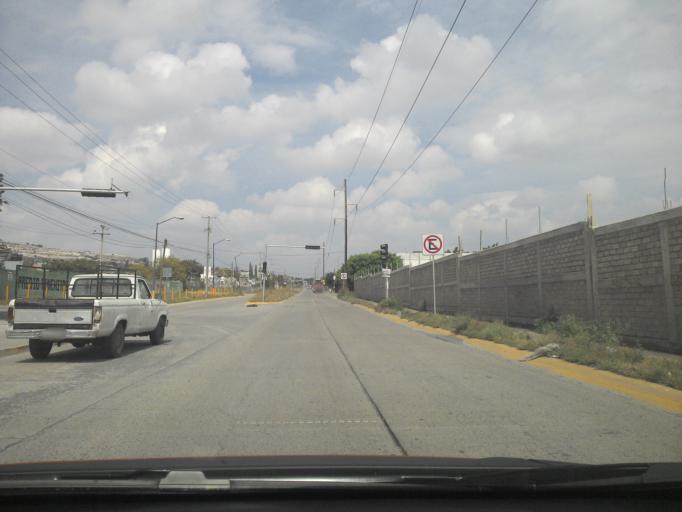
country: MX
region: Jalisco
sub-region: Tlajomulco de Zuniga
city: Altus Bosques
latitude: 20.5787
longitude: -103.3566
